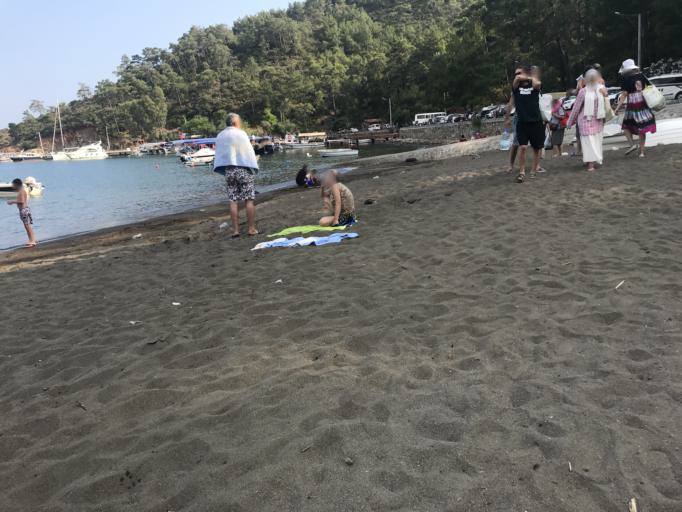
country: TR
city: Dalyan
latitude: 36.8297
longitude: 28.5485
